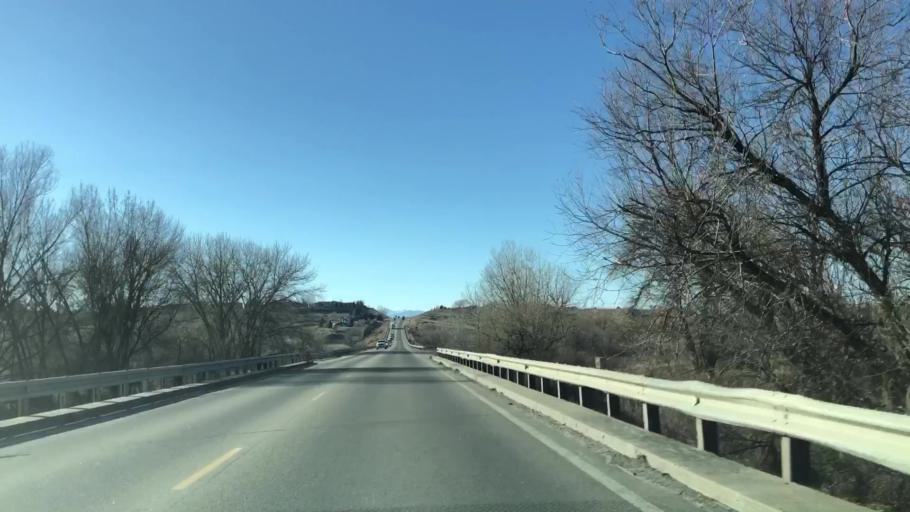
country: US
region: Colorado
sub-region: Weld County
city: Windsor
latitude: 40.4789
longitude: -104.9529
